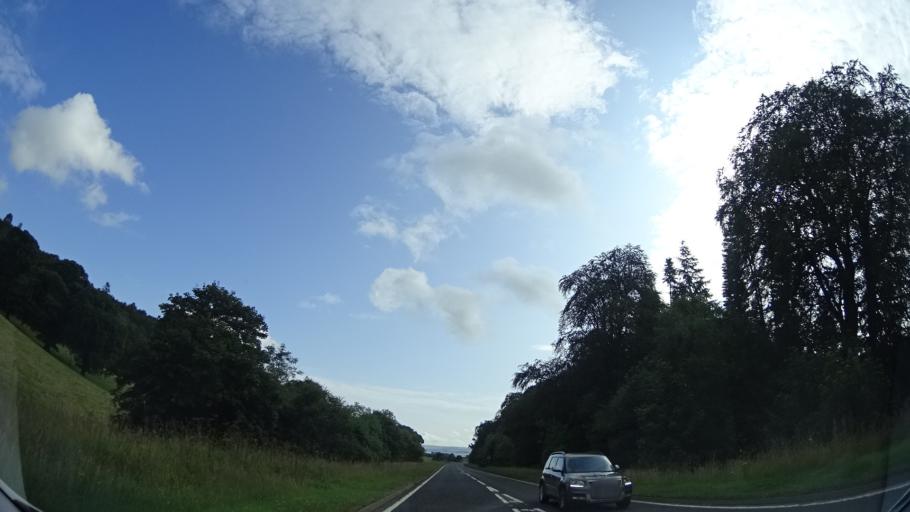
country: GB
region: Scotland
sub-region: Highland
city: Conon Bridge
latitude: 57.5690
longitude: -4.4659
